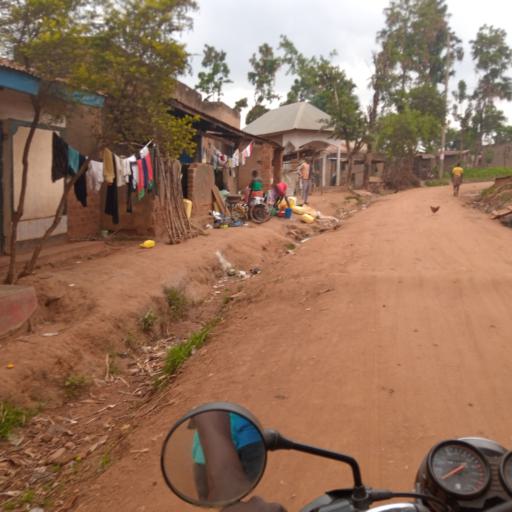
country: UG
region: Eastern Region
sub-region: Mbale District
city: Mbale
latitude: 1.1004
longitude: 34.1798
